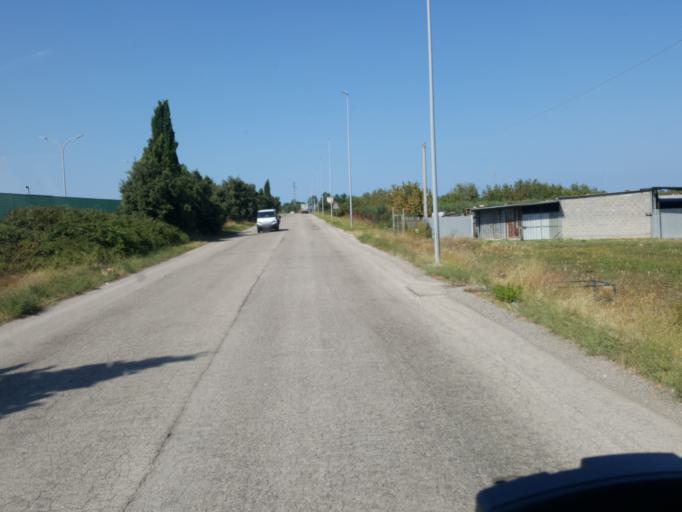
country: IT
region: Abruzzo
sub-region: Provincia di Chieti
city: Salvo Marina
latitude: 42.0630
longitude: 14.7625
